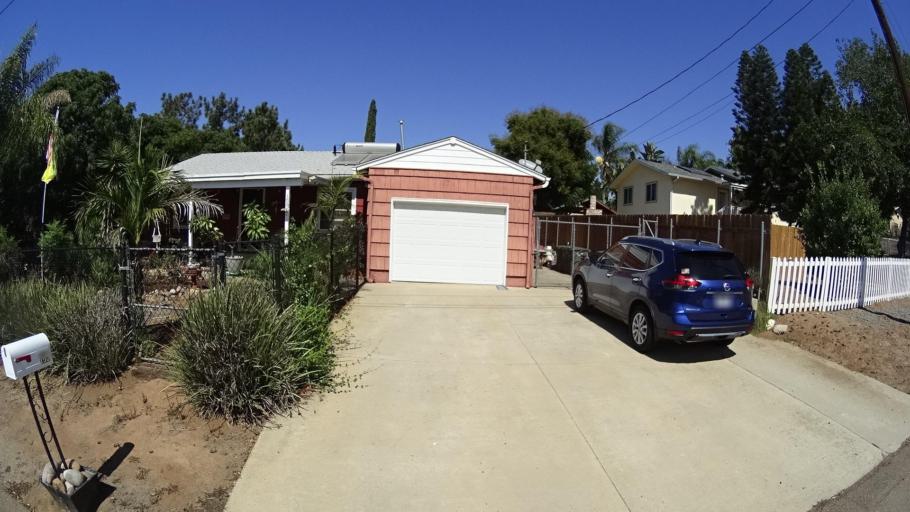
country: US
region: California
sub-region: San Diego County
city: Crest
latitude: 32.8073
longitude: -116.8638
